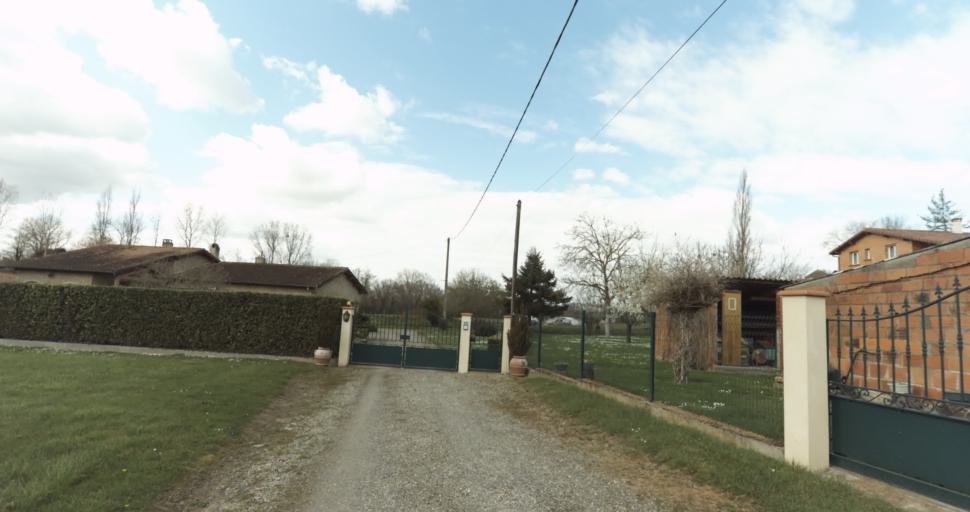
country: FR
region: Midi-Pyrenees
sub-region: Departement de la Haute-Garonne
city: Auterive
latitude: 43.3544
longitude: 1.4760
